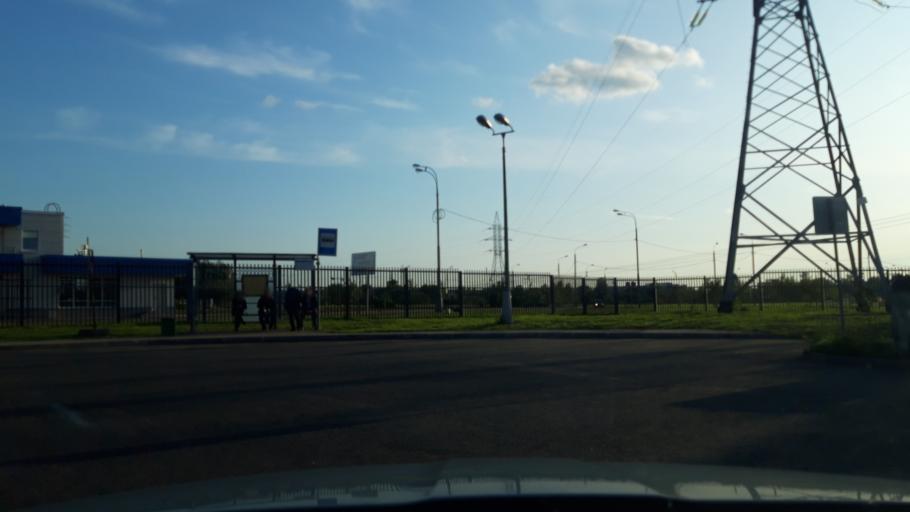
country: RU
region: Moskovskaya
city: Alabushevo
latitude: 56.0118
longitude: 37.1587
